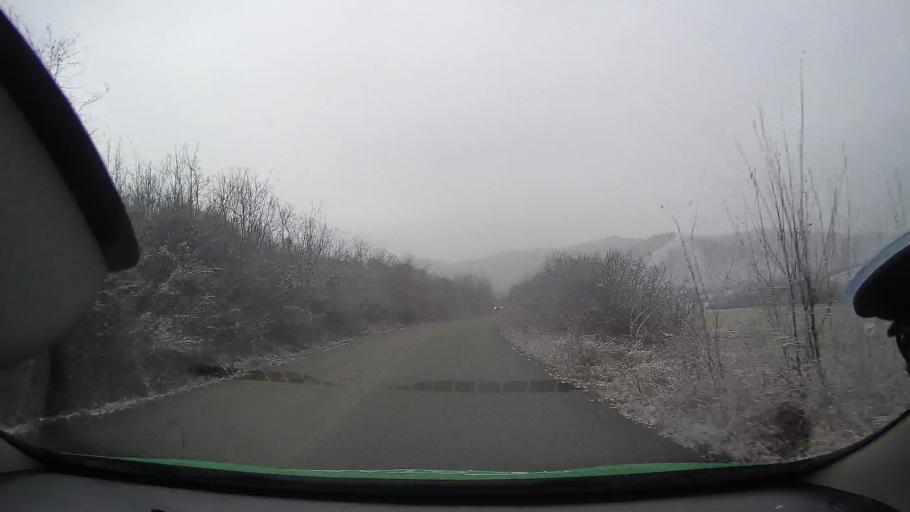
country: RO
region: Alba
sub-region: Comuna Hoparta
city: Hoparta
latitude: 46.3424
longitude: 23.9253
